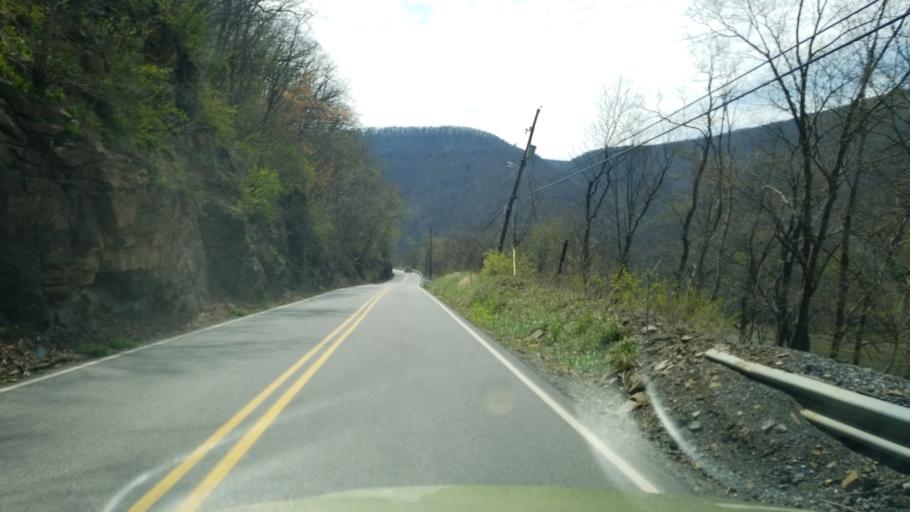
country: US
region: Pennsylvania
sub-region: Clinton County
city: Renovo
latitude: 41.3077
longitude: -77.8175
